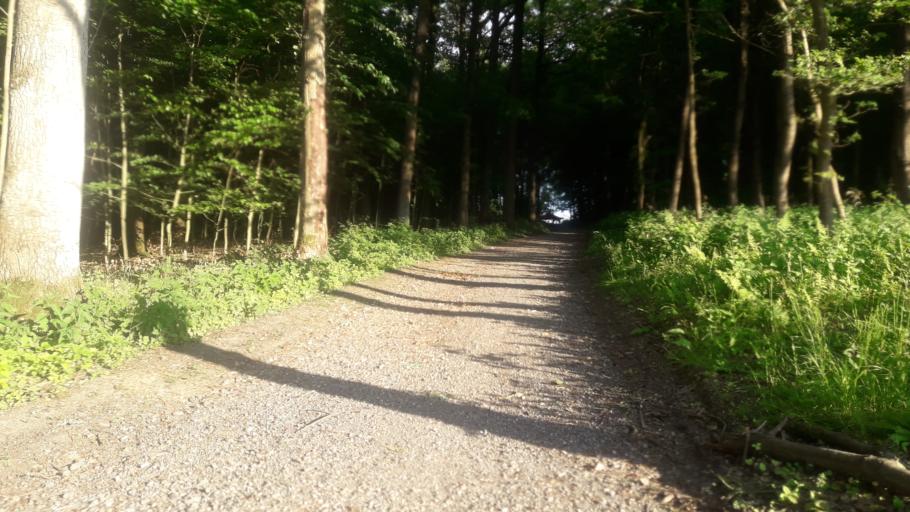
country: DE
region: North Rhine-Westphalia
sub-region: Regierungsbezirk Detmold
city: Paderborn
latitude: 51.6819
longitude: 8.7856
